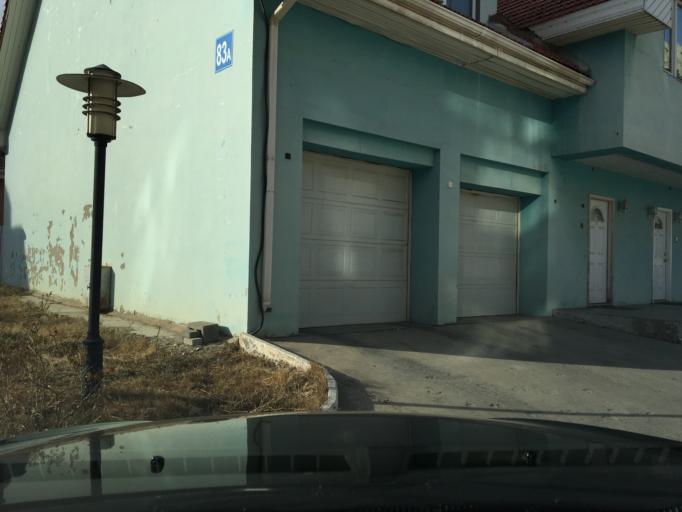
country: MN
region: Ulaanbaatar
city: Ulaanbaatar
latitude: 47.8941
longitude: 106.9190
